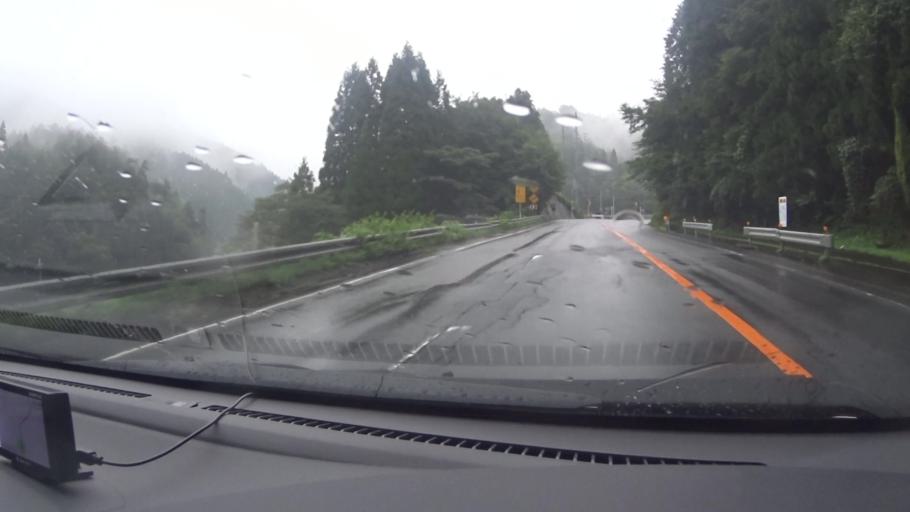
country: JP
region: Kyoto
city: Ayabe
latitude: 35.2436
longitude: 135.3098
